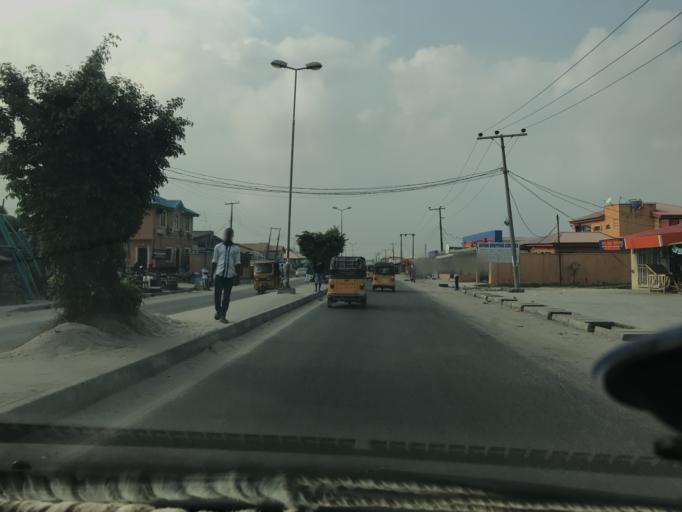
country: NG
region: Lagos
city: Ebute Ikorodu
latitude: 6.4932
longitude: 3.5823
